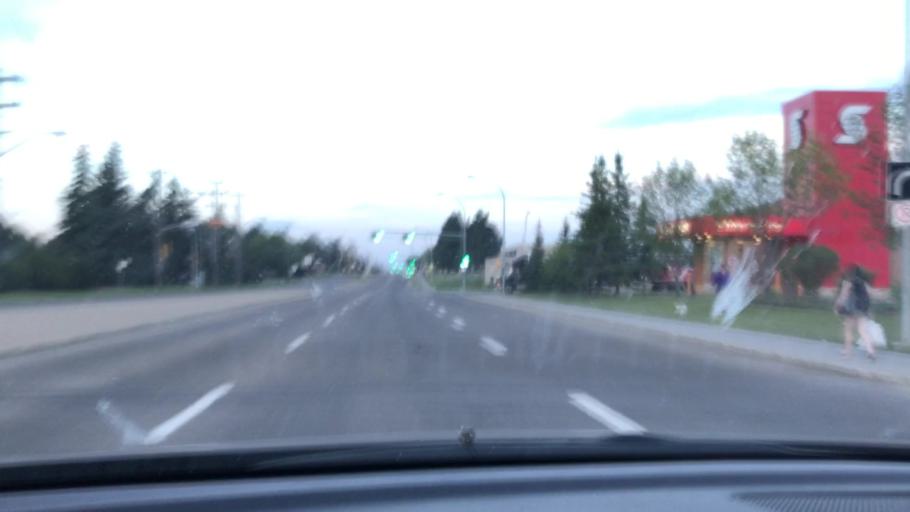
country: CA
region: Alberta
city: Edmonton
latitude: 53.4882
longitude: -113.5122
